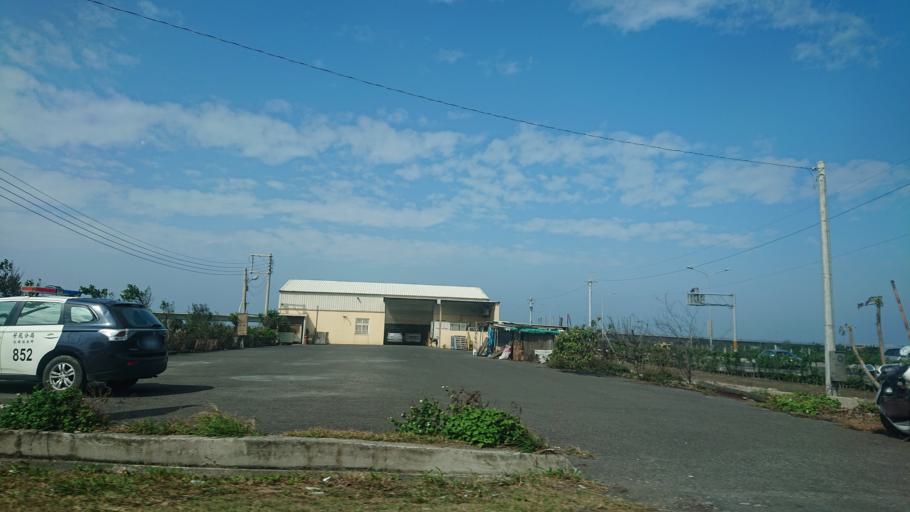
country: TW
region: Taiwan
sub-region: Changhua
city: Chang-hua
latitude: 23.9375
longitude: 120.3251
